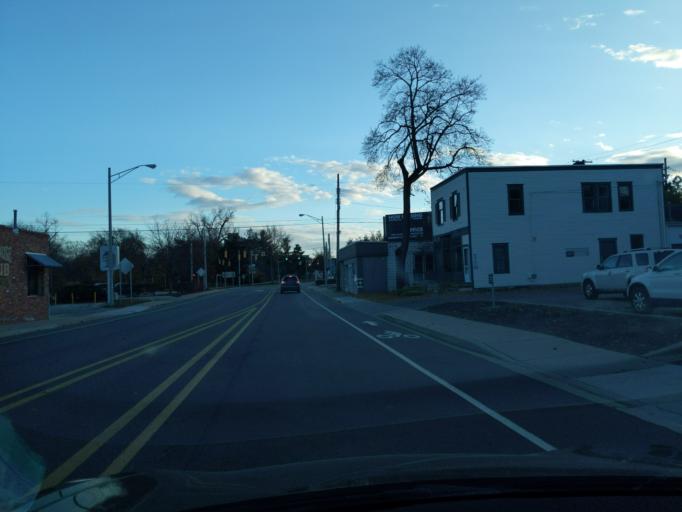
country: US
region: Michigan
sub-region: Ingham County
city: East Lansing
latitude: 42.7346
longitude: -84.4936
